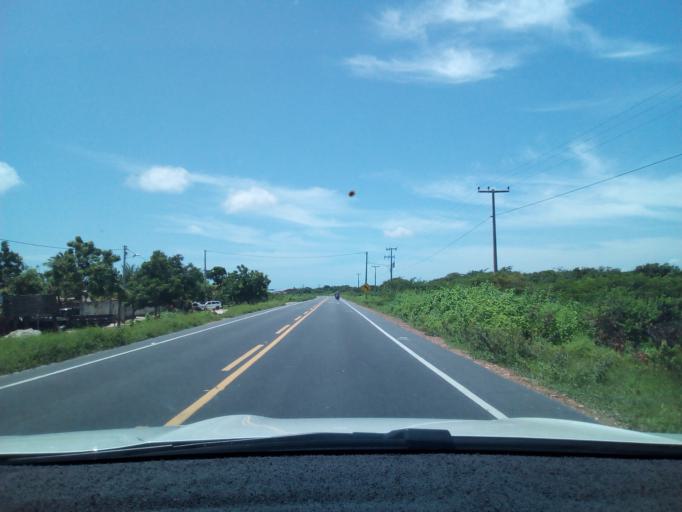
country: BR
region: Ceara
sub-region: Aracati
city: Aracati
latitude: -4.3935
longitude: -37.8690
